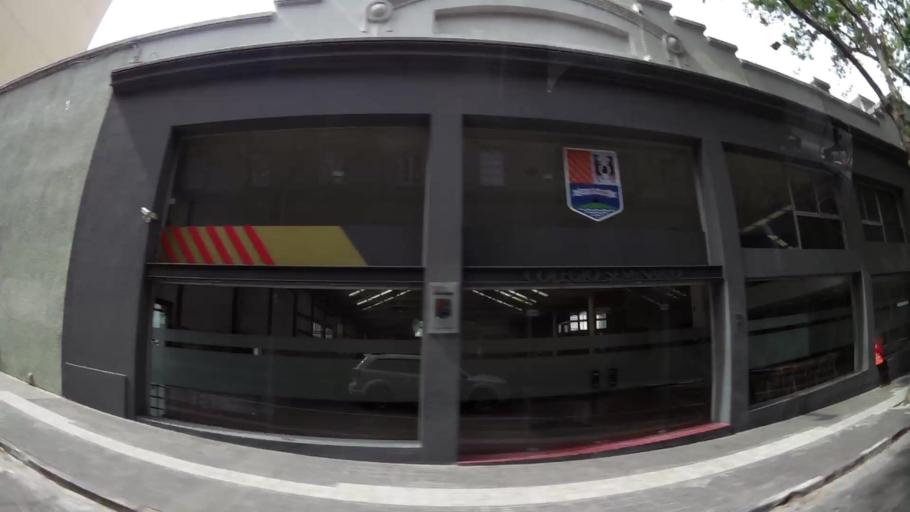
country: UY
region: Montevideo
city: Montevideo
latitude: -34.9082
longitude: -56.1838
